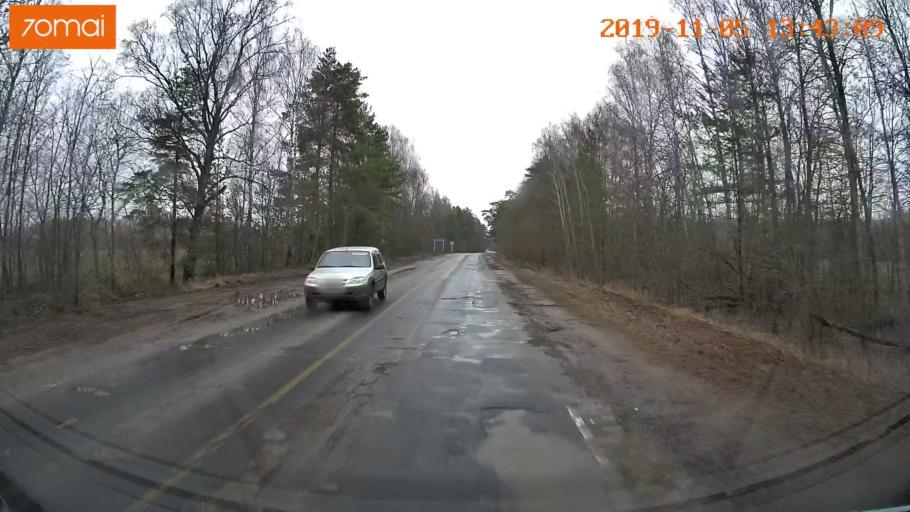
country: RU
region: Ivanovo
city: Shuya
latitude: 56.9716
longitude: 41.4006
